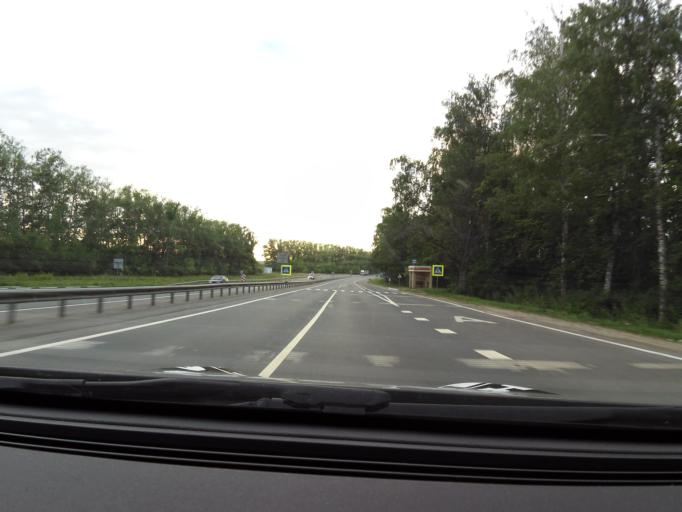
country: RU
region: Chuvashia
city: Kugesi
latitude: 56.0118
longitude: 47.3130
